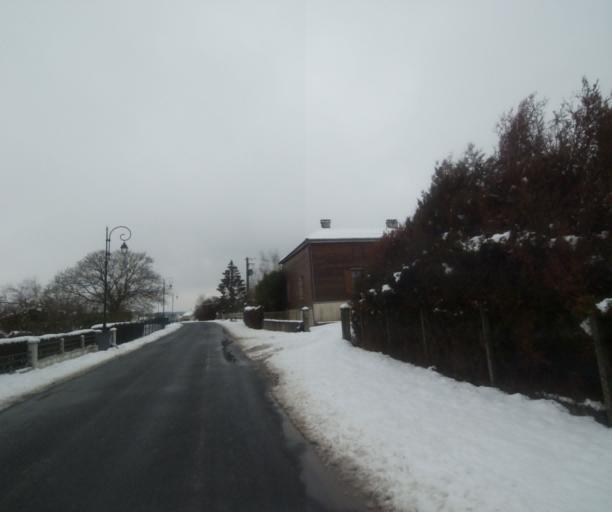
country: FR
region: Champagne-Ardenne
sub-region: Departement de la Haute-Marne
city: Montier-en-Der
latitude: 48.5190
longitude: 4.8195
